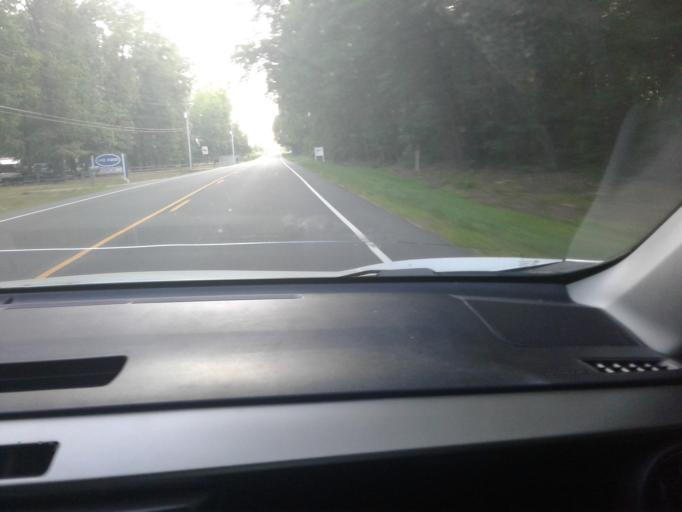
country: US
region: North Carolina
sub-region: Wake County
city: Fuquay-Varina
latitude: 35.5172
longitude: -78.8132
